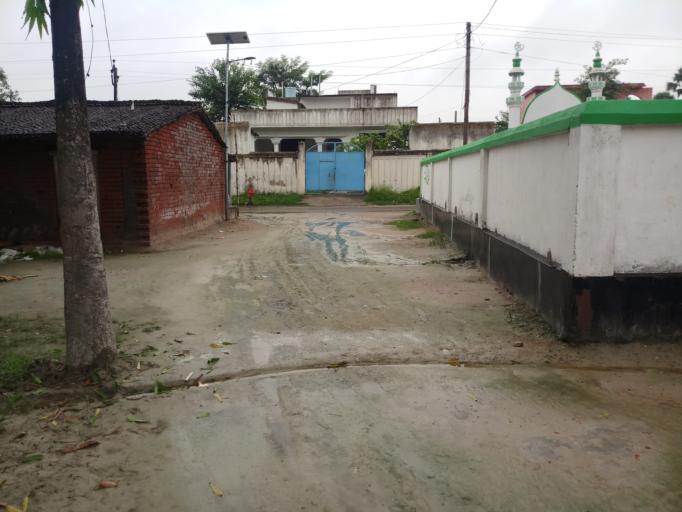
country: IN
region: Bihar
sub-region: Vaishali
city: Lalganj
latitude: 25.8466
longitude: 85.2599
